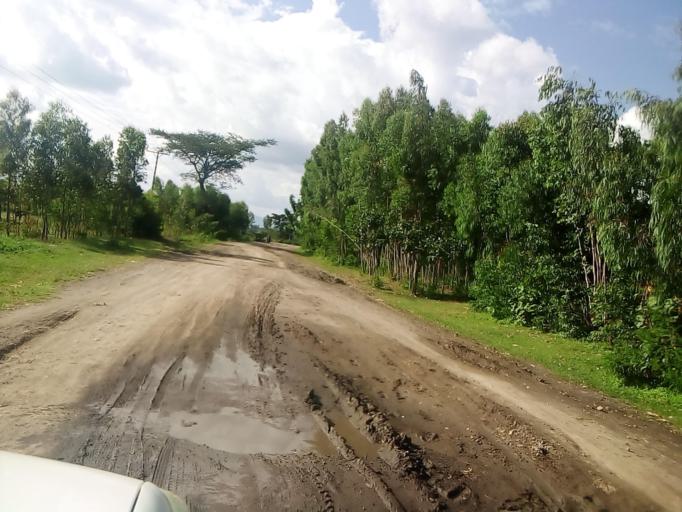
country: ET
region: Southern Nations, Nationalities, and People's Region
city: K'olito
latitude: 7.6558
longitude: 38.0486
